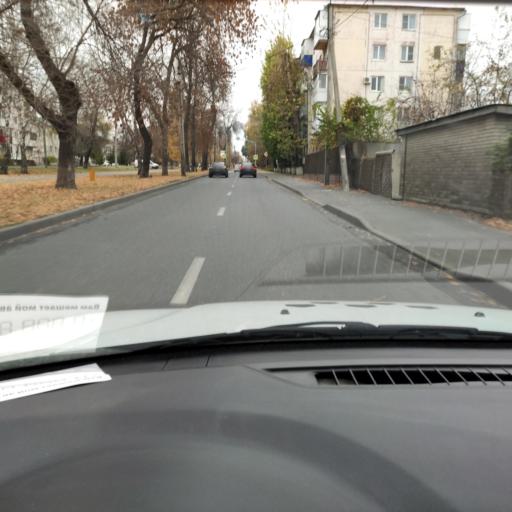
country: RU
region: Samara
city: Tol'yatti
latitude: 53.5220
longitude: 49.3993
